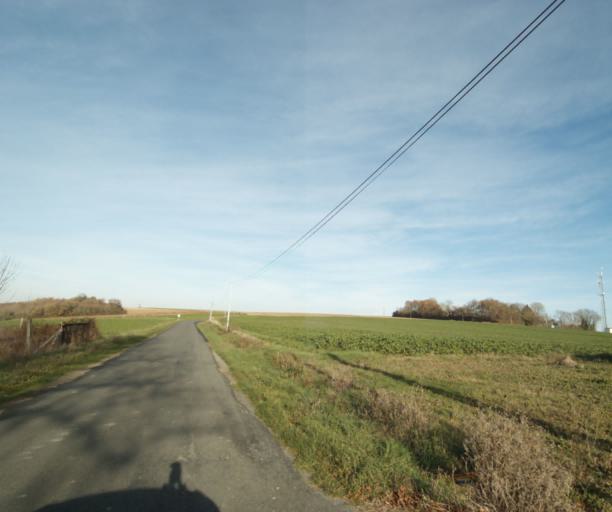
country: FR
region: Poitou-Charentes
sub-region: Departement de la Charente-Maritime
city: Chaniers
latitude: 45.7141
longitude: -0.5309
